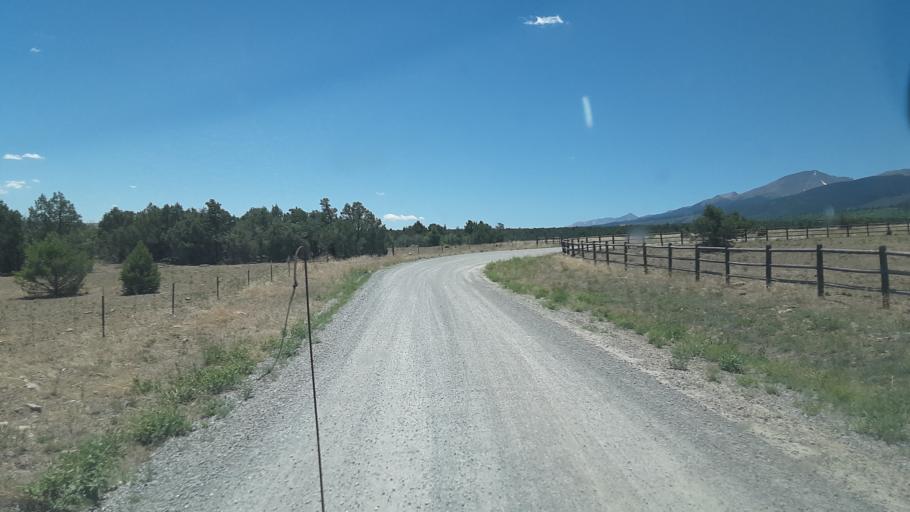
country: US
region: Colorado
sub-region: Custer County
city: Westcliffe
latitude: 38.3126
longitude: -105.6707
